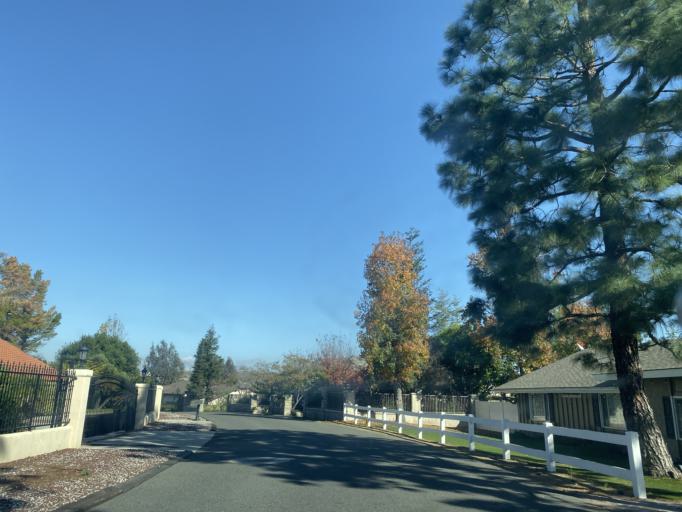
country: US
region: California
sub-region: Orange County
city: Villa Park
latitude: 33.8061
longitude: -117.7720
